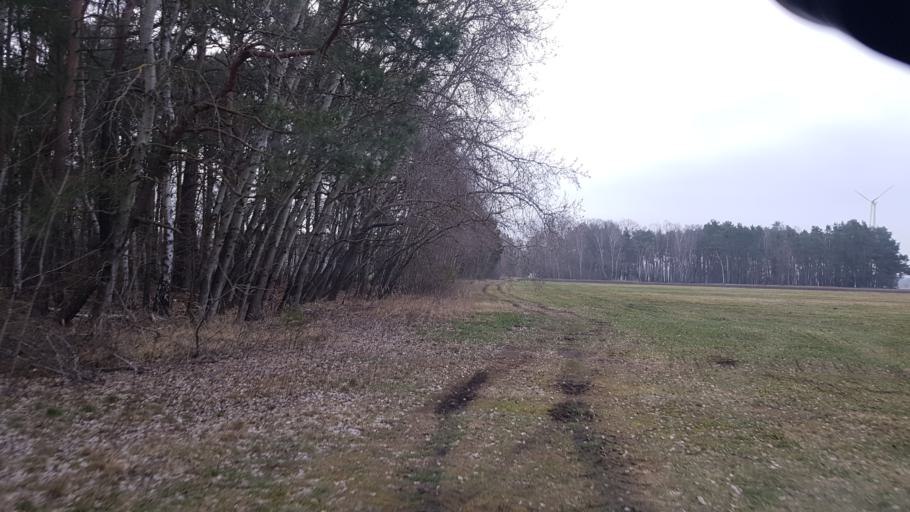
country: DE
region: Brandenburg
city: Schonborn
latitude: 51.6031
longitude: 13.5077
